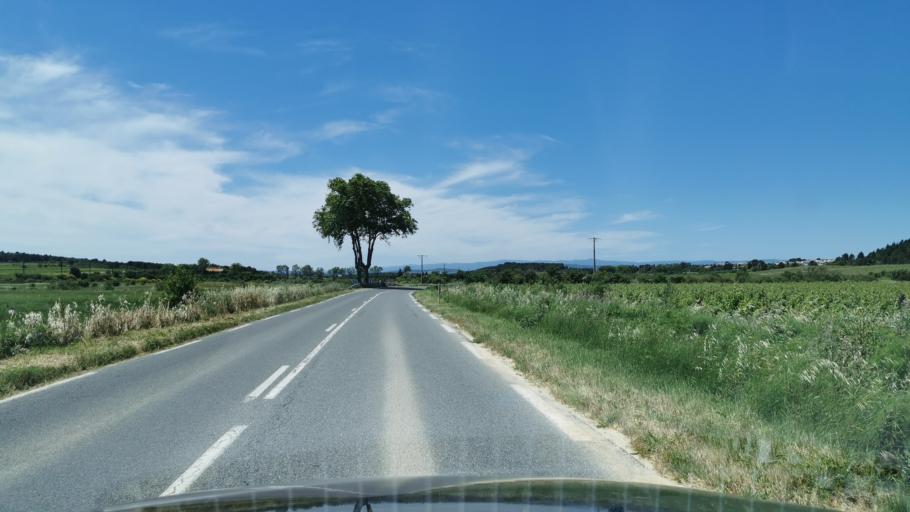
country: FR
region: Languedoc-Roussillon
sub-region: Departement de l'Aude
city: Marcorignan
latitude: 43.2126
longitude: 2.9375
